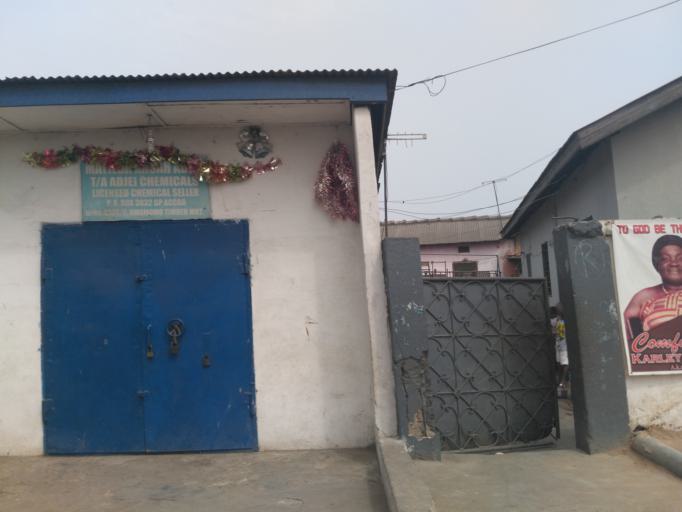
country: GH
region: Greater Accra
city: Accra
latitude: 5.5422
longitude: -0.2156
